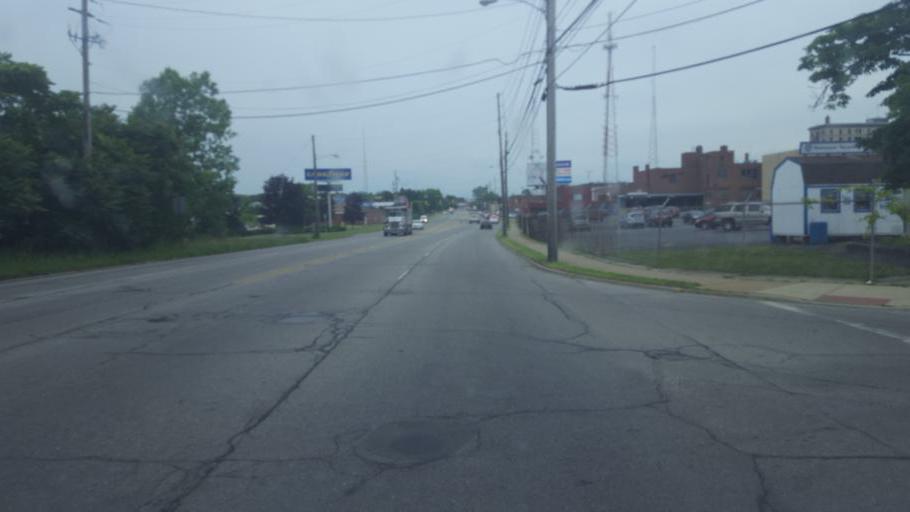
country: US
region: Ohio
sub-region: Trumbull County
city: Warren
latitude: 41.2342
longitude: -80.8135
